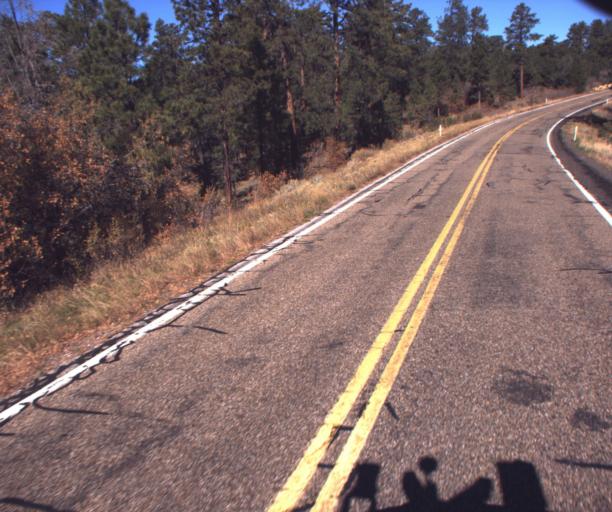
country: US
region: Arizona
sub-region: Coconino County
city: Fredonia
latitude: 36.7772
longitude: -112.2560
